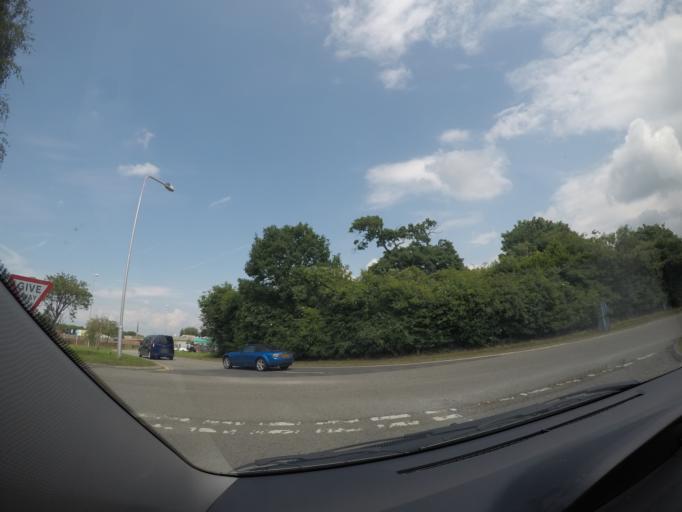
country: GB
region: England
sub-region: Cumbria
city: Scotby
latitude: 54.7969
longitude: -2.8725
